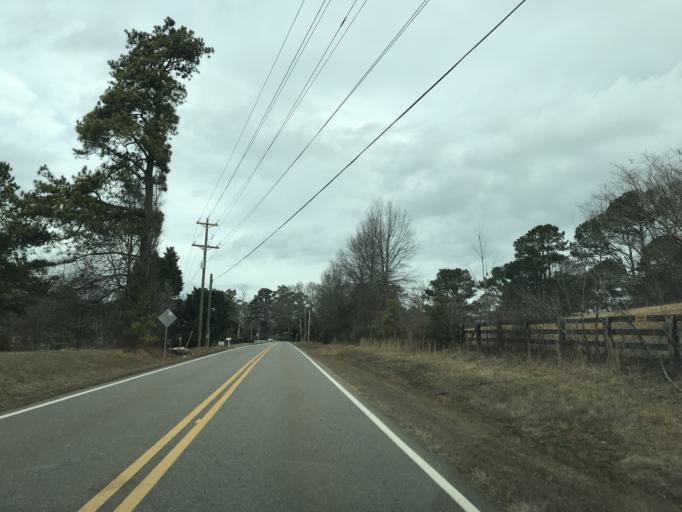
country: US
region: Georgia
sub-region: Fulton County
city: Milton
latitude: 34.1918
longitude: -84.3417
